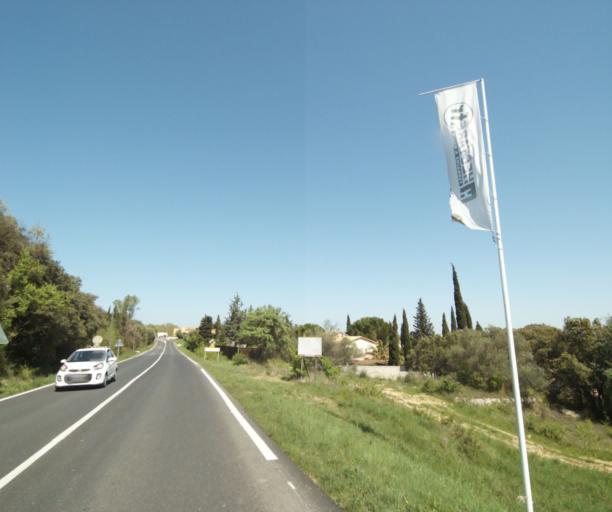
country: FR
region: Languedoc-Roussillon
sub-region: Departement de l'Herault
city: Restinclieres
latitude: 43.7193
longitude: 4.0349
